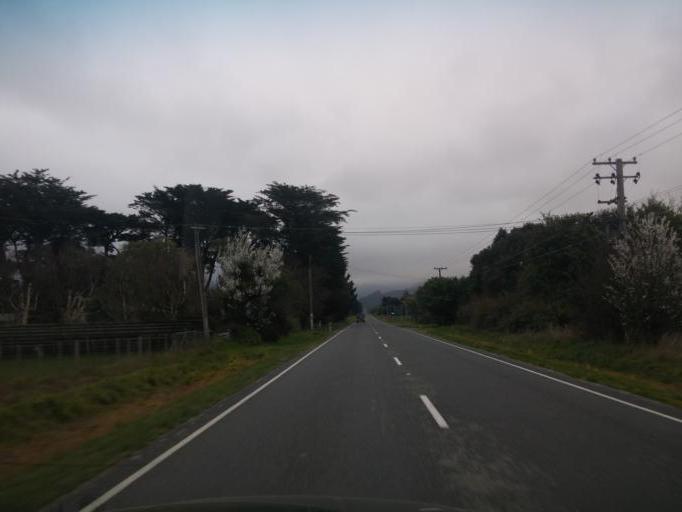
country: NZ
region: Wellington
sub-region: Upper Hutt City
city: Upper Hutt
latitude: -41.1326
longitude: 175.3496
